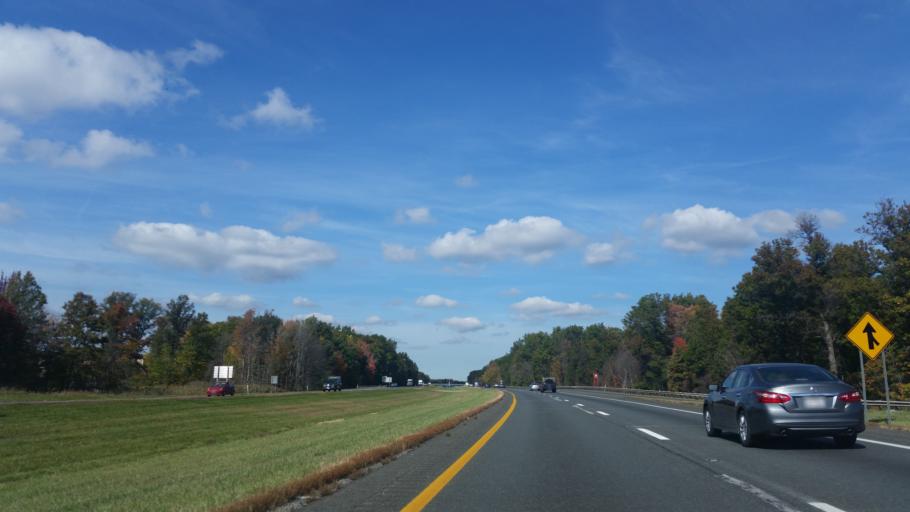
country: US
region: Ohio
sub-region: Cuyahoga County
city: Brecksville
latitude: 41.2912
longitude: -81.6373
